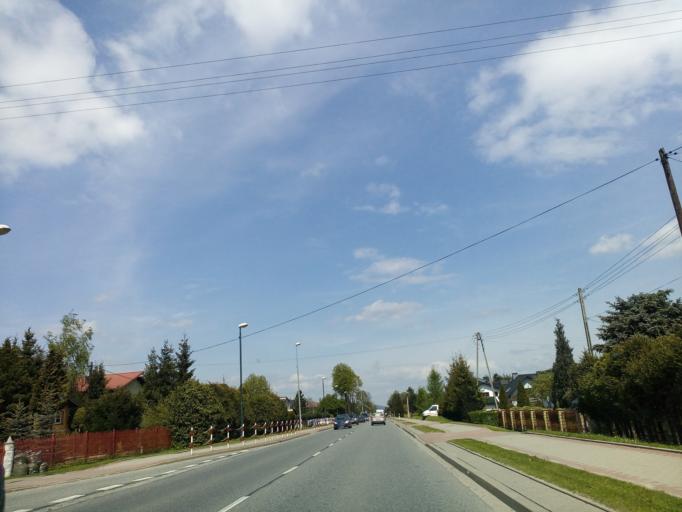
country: PL
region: Lesser Poland Voivodeship
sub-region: Powiat nowosadecki
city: Nawojowa
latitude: 49.5670
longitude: 20.7393
